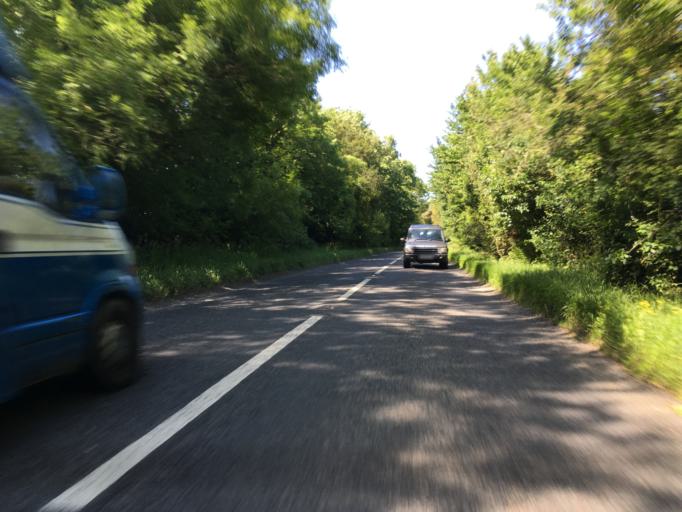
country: GB
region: England
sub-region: Gloucestershire
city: Stow on the Wold
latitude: 51.9327
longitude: -1.6697
